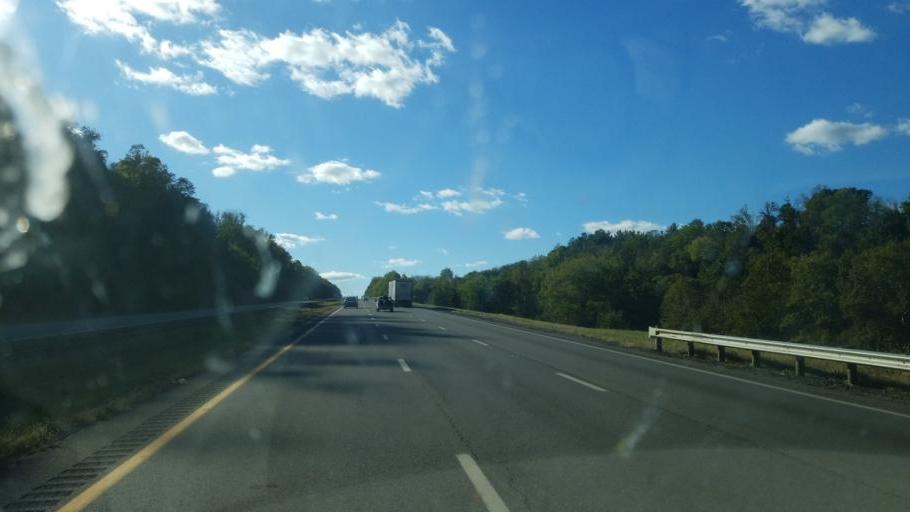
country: US
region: Ohio
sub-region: Belmont County
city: Wolfhurst
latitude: 40.0467
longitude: -80.7685
